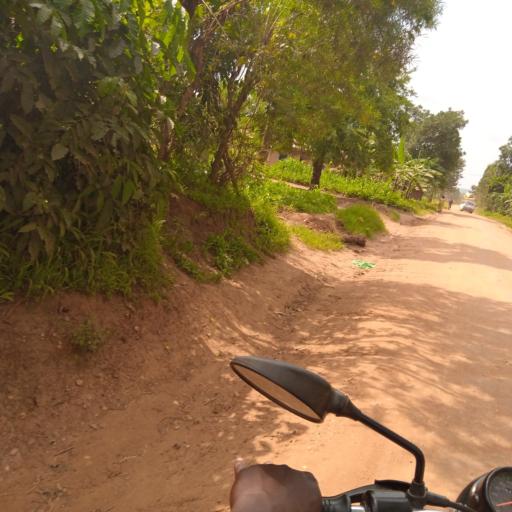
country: UG
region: Eastern Region
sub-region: Mbale District
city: Mbale
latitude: 1.1088
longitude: 34.2013
